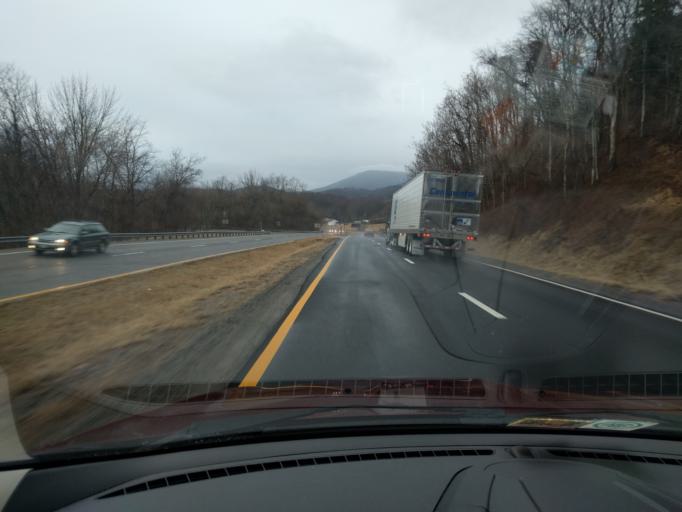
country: US
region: Virginia
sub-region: Giles County
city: Pembroke
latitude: 37.3177
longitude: -80.5884
